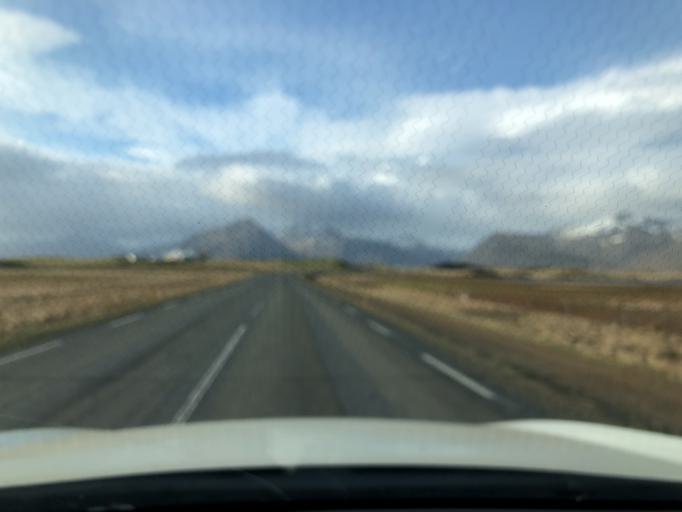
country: IS
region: East
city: Hoefn
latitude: 64.2723
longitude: -15.2022
